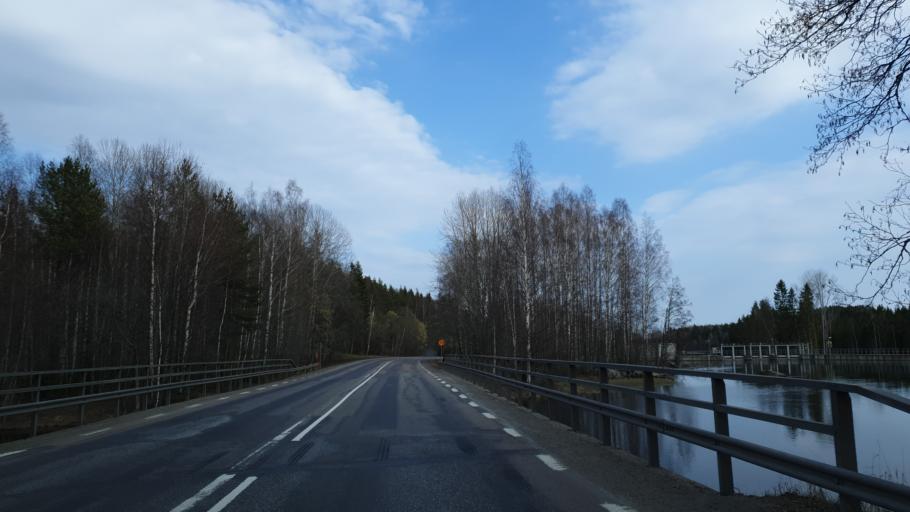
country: SE
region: Gaevleborg
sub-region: Hudiksvalls Kommun
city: Iggesund
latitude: 61.6503
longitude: 17.0345
